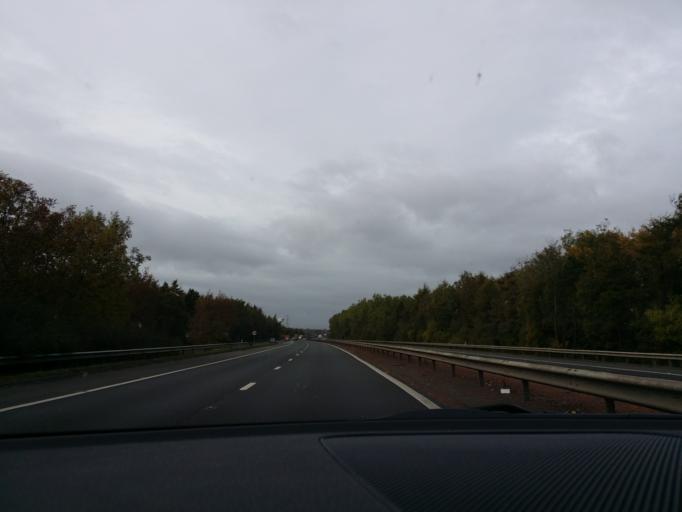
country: GB
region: Scotland
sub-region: Falkirk
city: Grangemouth
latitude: 56.0138
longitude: -3.7465
